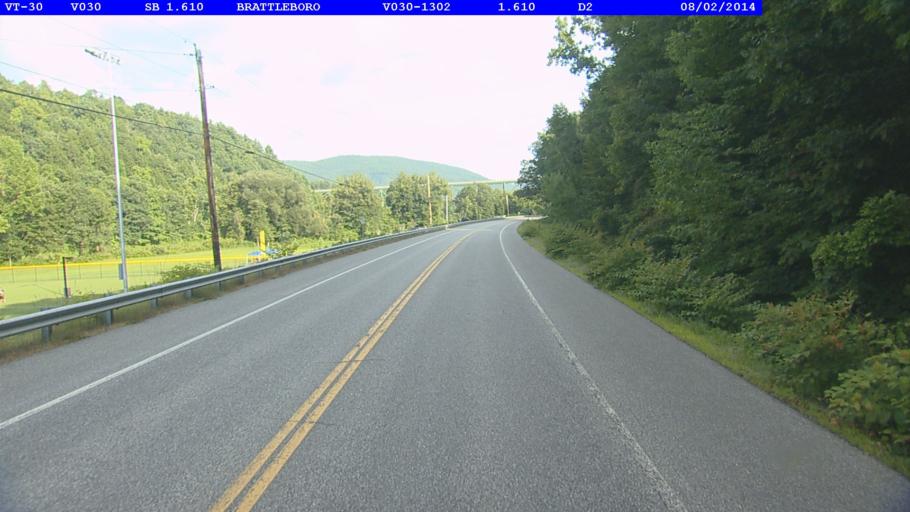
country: US
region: Vermont
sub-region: Windham County
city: Brattleboro
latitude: 42.8777
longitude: -72.5744
